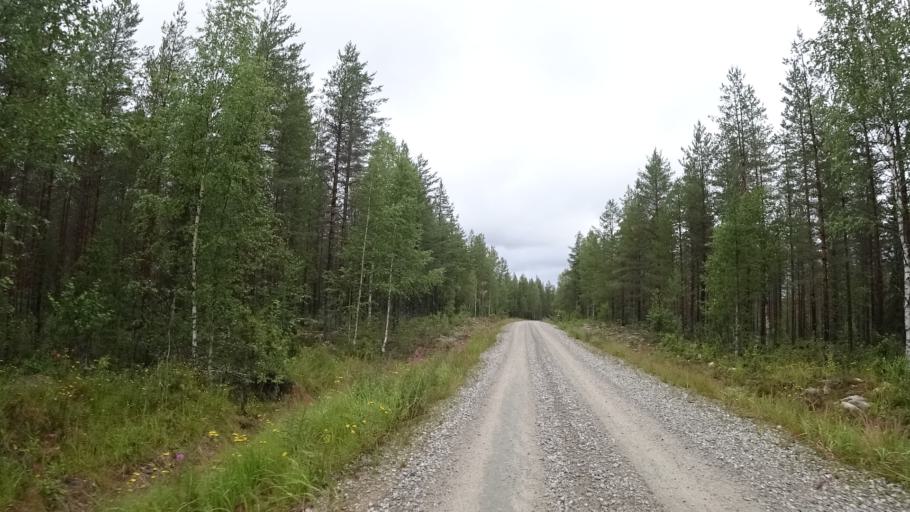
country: FI
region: North Karelia
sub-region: Pielisen Karjala
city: Lieksa
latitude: 63.4766
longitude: 30.2603
